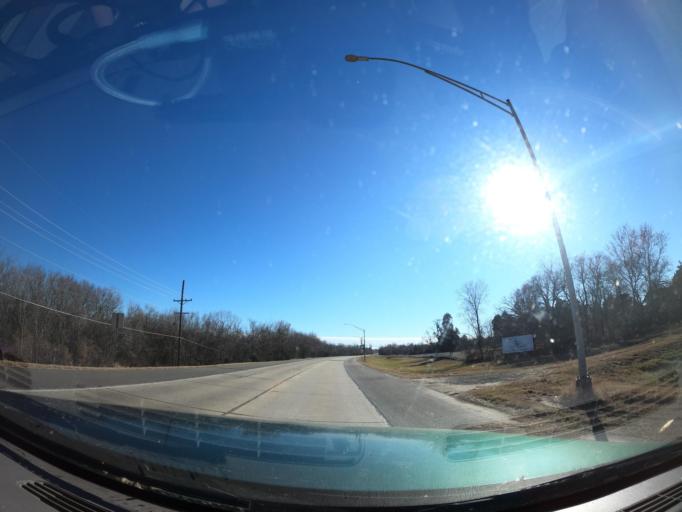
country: US
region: Oklahoma
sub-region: McIntosh County
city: Eufaula
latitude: 35.2963
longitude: -95.5824
